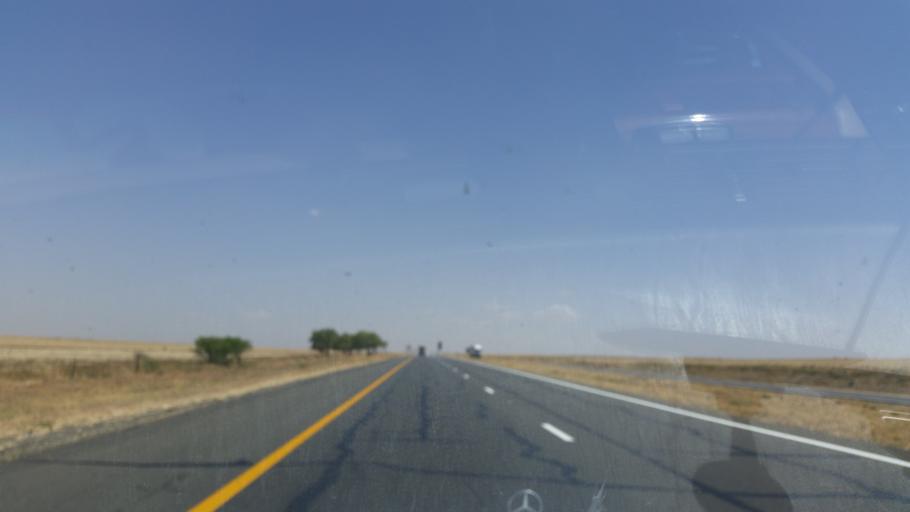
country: ZA
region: Orange Free State
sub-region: Lejweleputswa District Municipality
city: Brandfort
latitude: -28.8679
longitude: 26.5287
